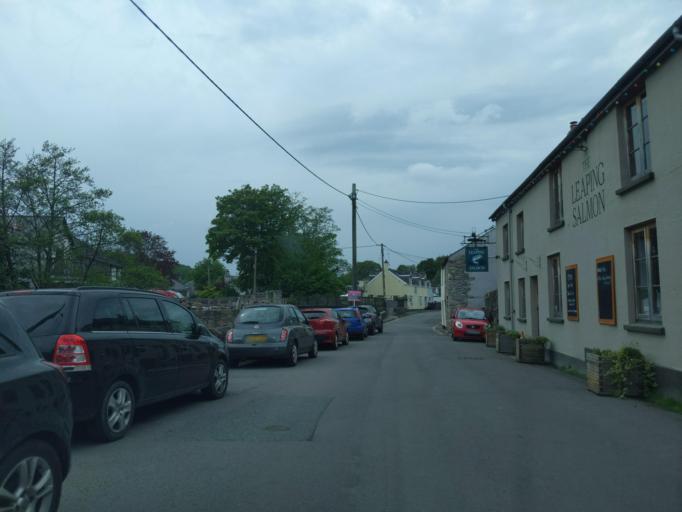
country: GB
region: England
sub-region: Devon
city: Horrabridge
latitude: 50.5104
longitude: -4.0983
